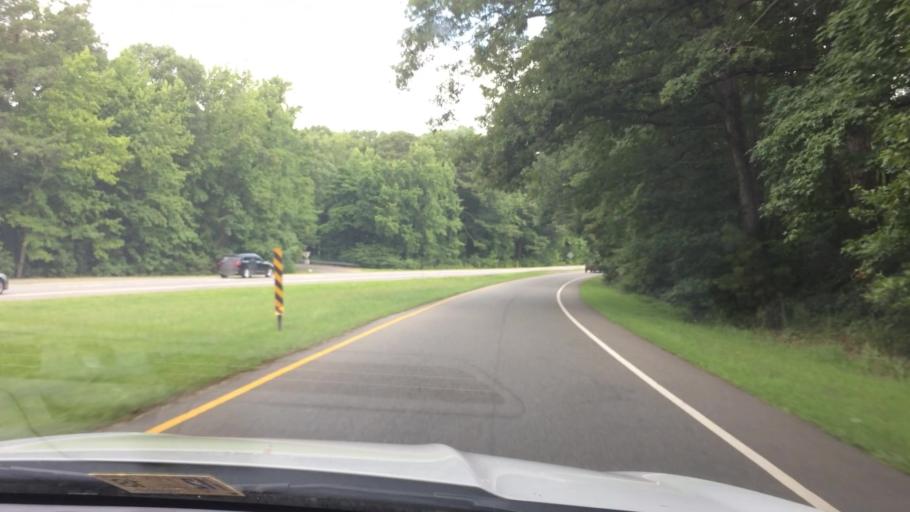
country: US
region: Virginia
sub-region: City of Poquoson
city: Poquoson
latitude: 37.1282
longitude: -76.4586
